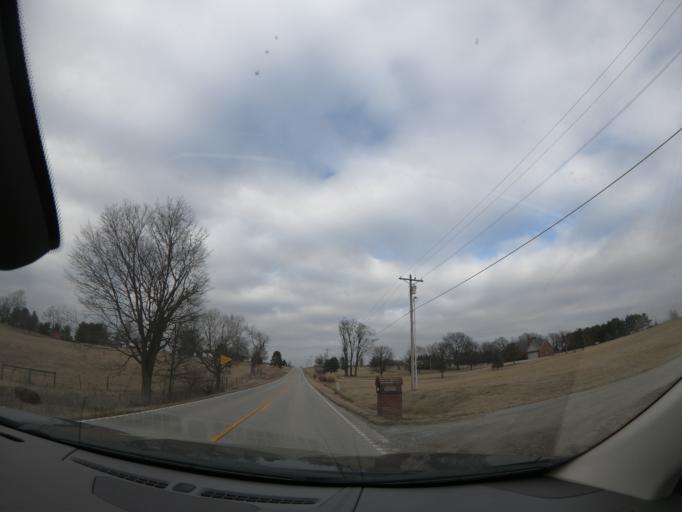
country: US
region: Kentucky
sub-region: Nelson County
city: Bardstown
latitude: 37.8581
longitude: -85.3386
